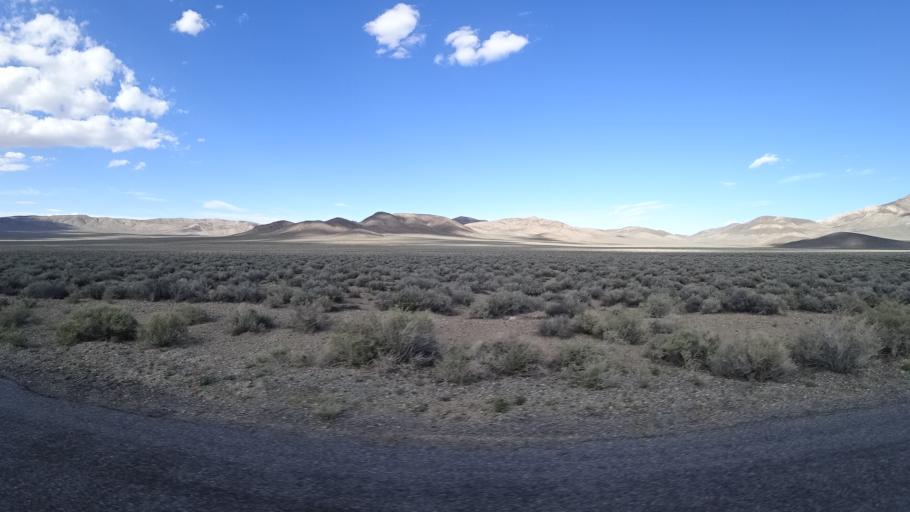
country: US
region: California
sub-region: San Bernardino County
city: Searles Valley
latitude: 36.3684
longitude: -117.1383
